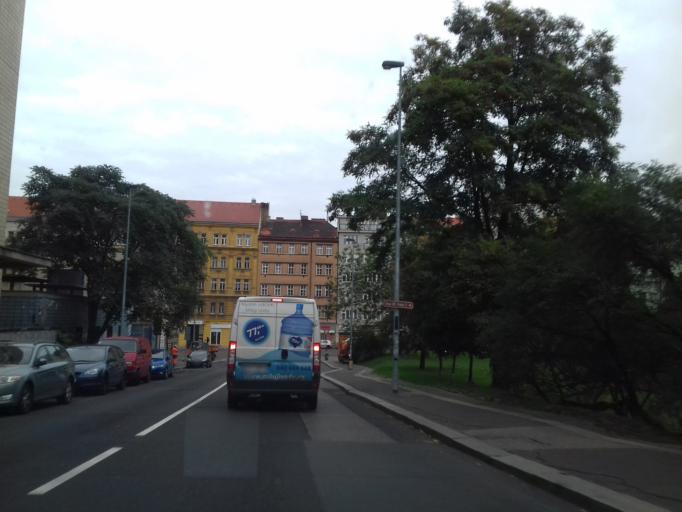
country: CZ
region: Praha
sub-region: Praha 8
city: Karlin
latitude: 50.0843
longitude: 14.4433
